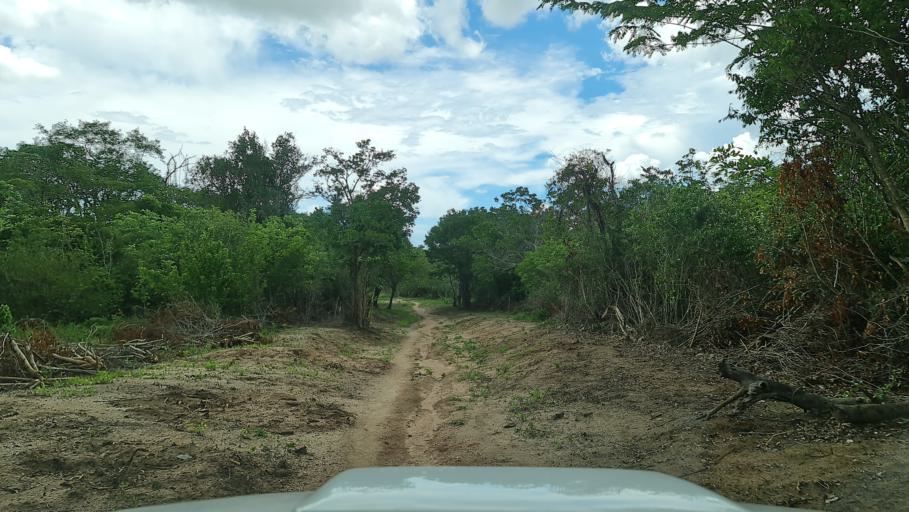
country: MZ
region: Nampula
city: Ilha de Mocambique
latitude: -15.5001
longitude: 40.1725
